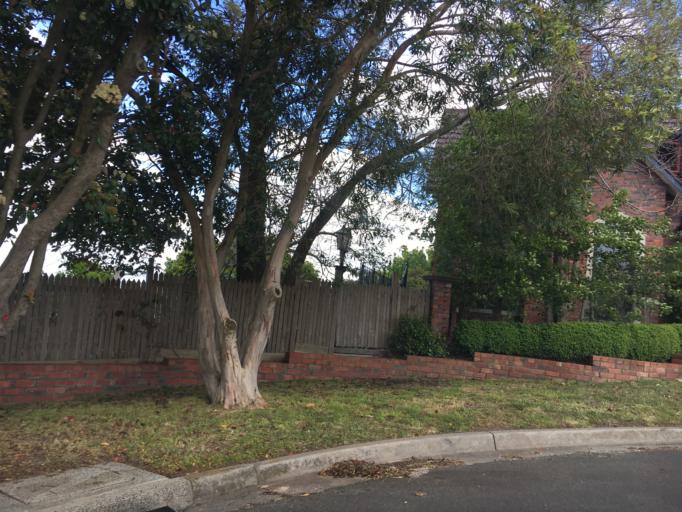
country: AU
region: Victoria
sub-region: Monash
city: Mulgrave
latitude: -37.8914
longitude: 145.1775
